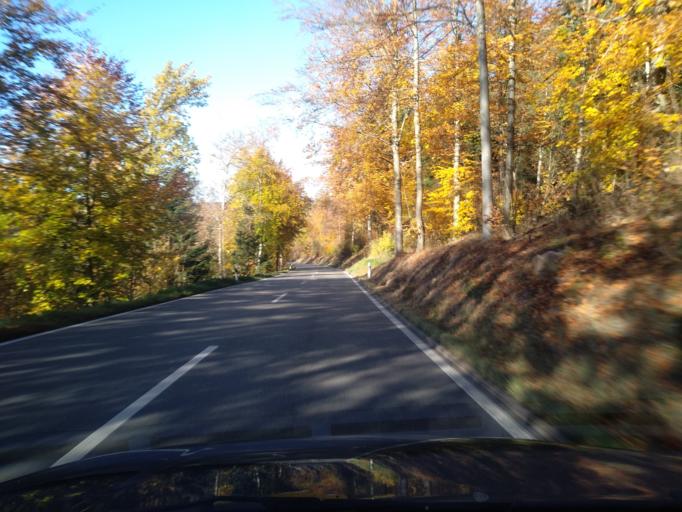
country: DE
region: Baden-Wuerttemberg
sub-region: Karlsruhe Region
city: Bad Liebenzell
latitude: 48.7727
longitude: 8.7430
